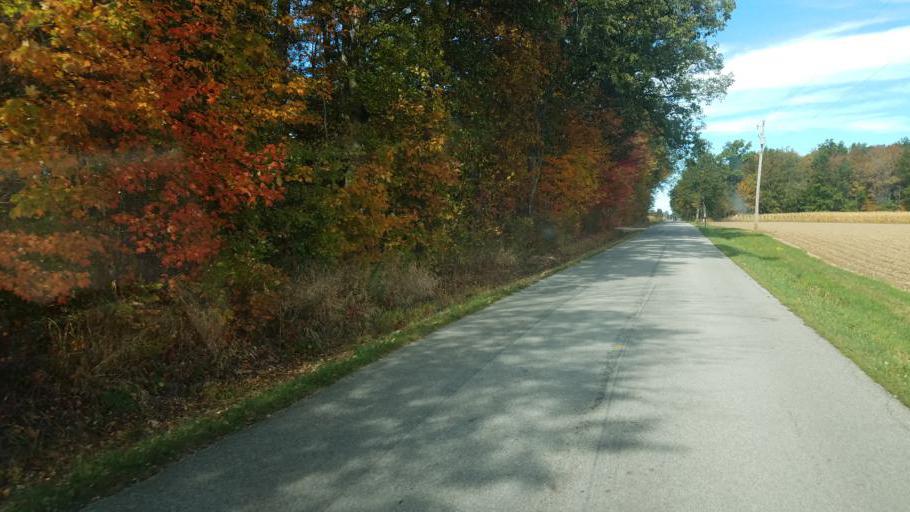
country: US
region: Ohio
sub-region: Huron County
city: Wakeman
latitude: 41.2096
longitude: -82.4598
